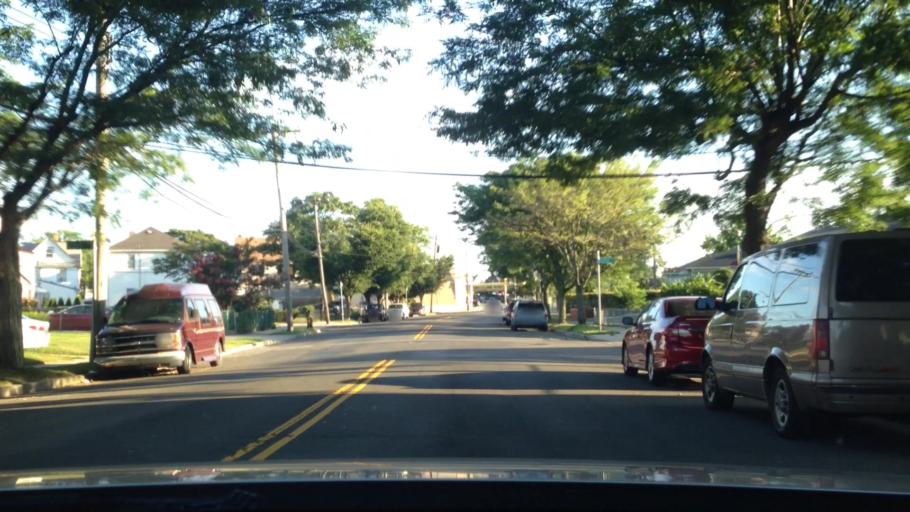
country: US
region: New York
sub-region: Nassau County
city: South Valley Stream
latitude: 40.6637
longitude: -73.7295
